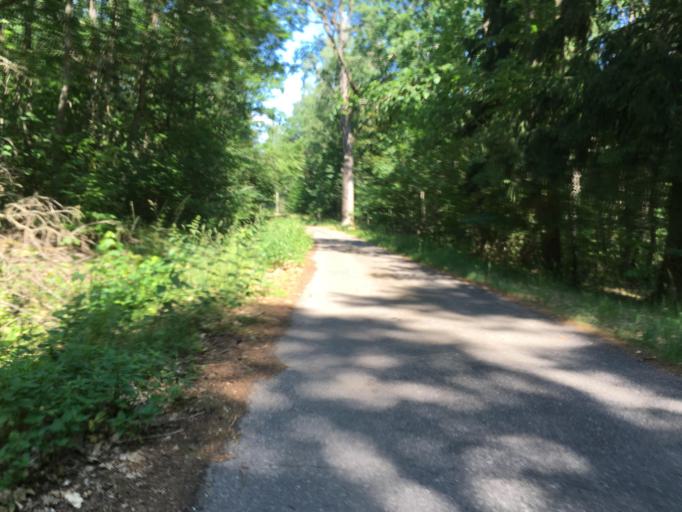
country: DE
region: Brandenburg
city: Marienwerder
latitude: 52.9145
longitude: 13.6662
